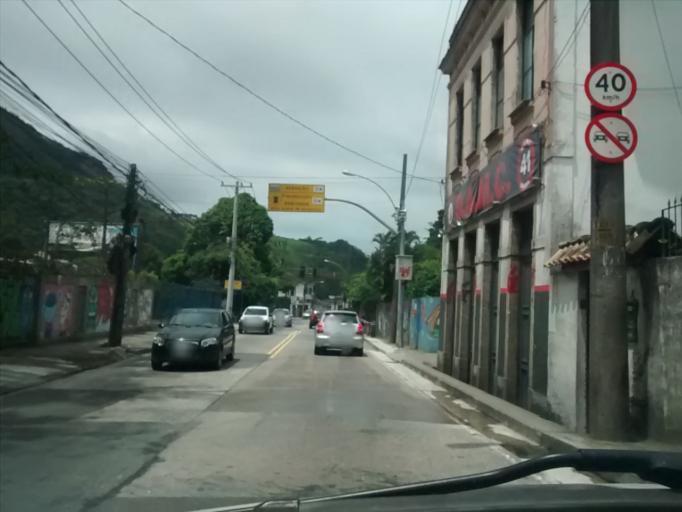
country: BR
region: Rio de Janeiro
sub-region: Rio De Janeiro
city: Rio de Janeiro
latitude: -22.9719
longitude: -43.2835
